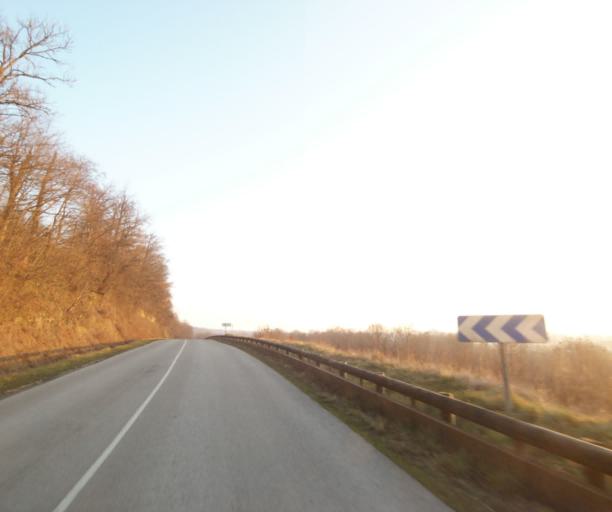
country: FR
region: Champagne-Ardenne
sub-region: Departement de la Haute-Marne
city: Bienville
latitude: 48.5902
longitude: 5.0423
